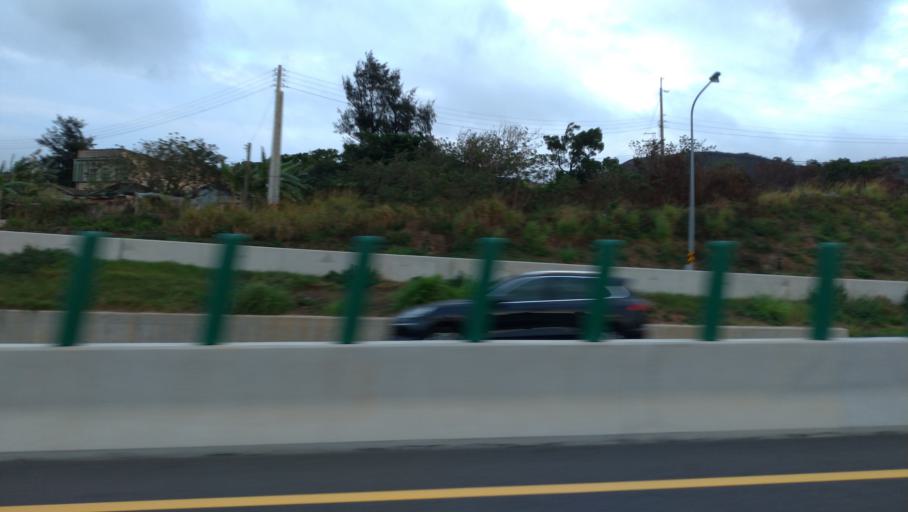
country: TW
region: Taiwan
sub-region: Miaoli
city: Miaoli
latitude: 24.5413
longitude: 120.7008
